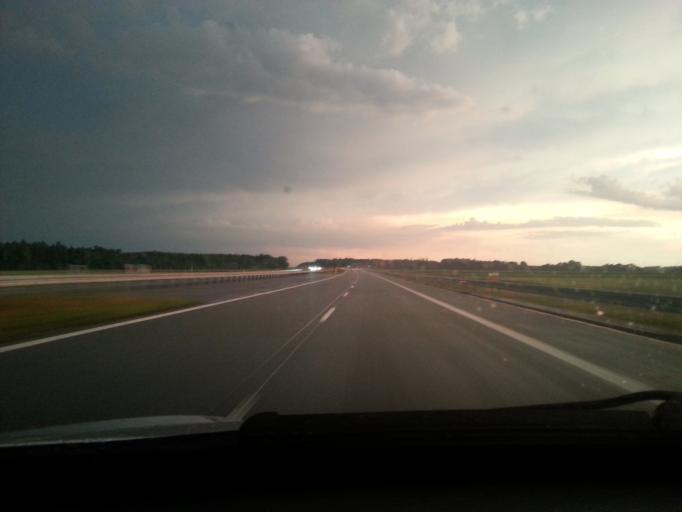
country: PL
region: Lodz Voivodeship
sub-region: Powiat pabianicki
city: Dobron
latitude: 51.5888
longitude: 19.2075
